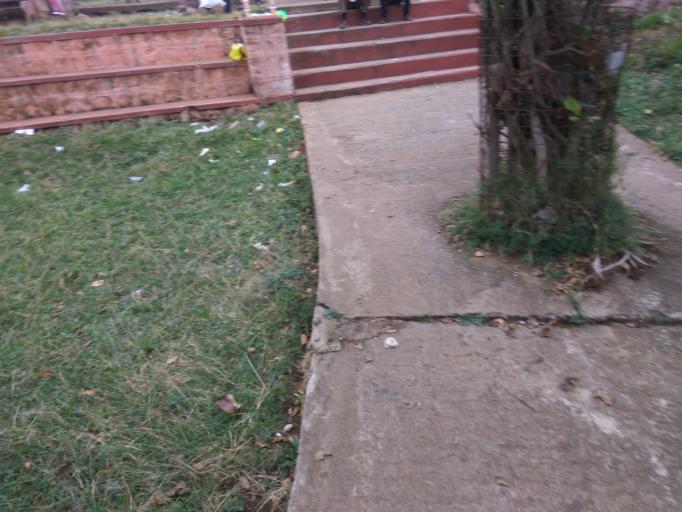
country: IN
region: Tamil Nadu
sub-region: Salem
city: Salem
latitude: 11.7666
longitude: 78.2393
